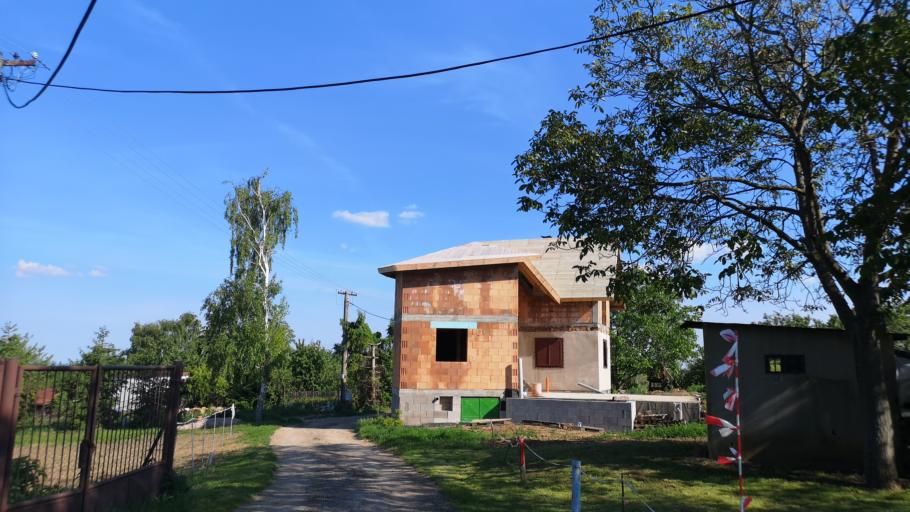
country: SK
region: Nitriansky
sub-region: Okres Nitra
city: Nitra
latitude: 48.2553
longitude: 18.0826
